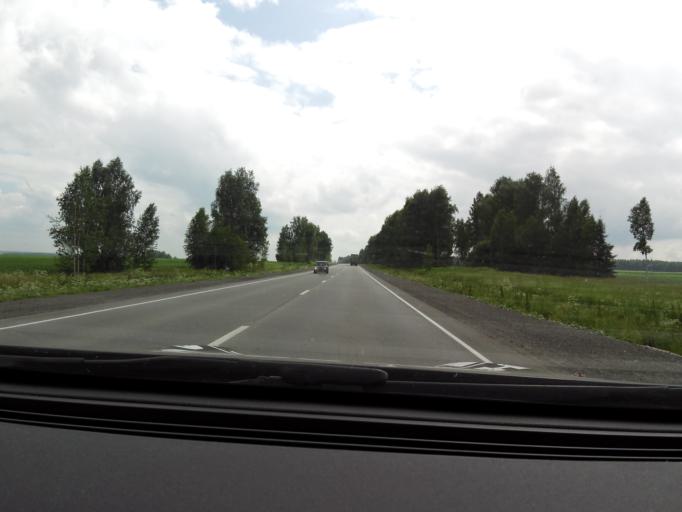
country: RU
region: Perm
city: Suksun
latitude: 56.9709
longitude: 57.5177
